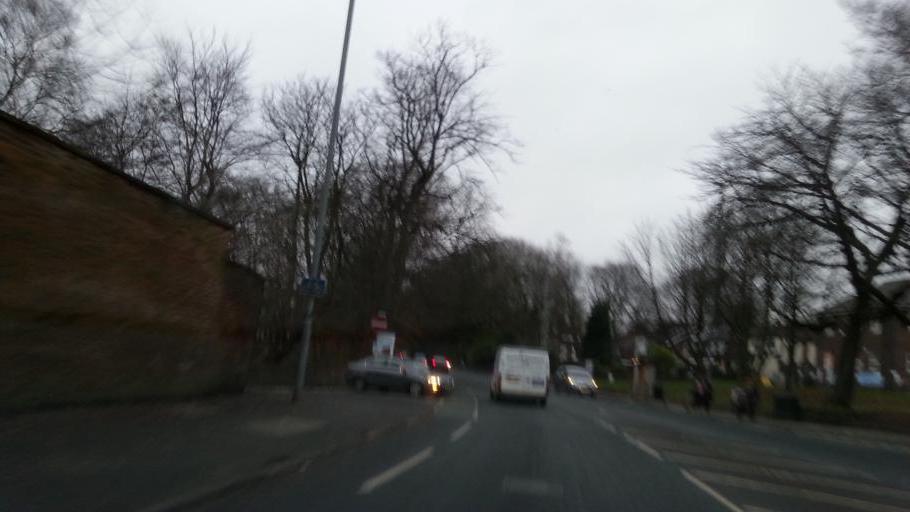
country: GB
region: England
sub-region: Manchester
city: Crumpsall
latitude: 53.5120
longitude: -2.2637
